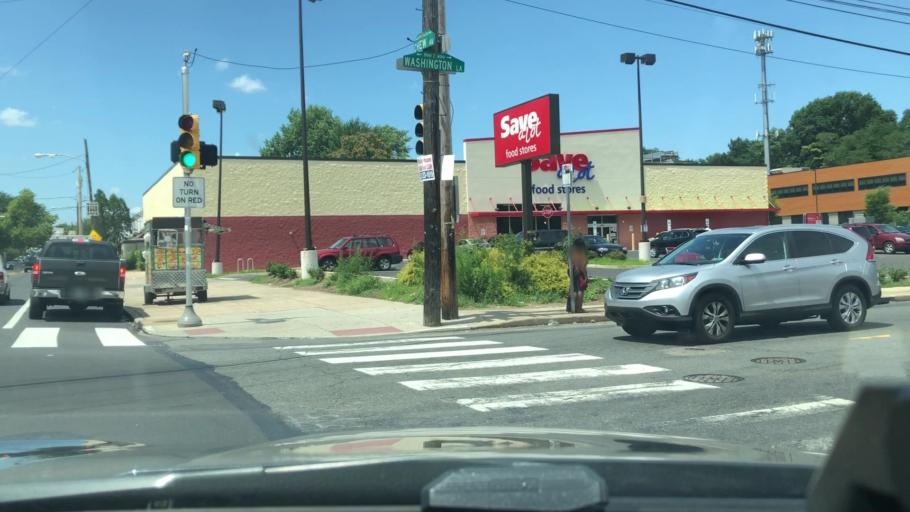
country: US
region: Pennsylvania
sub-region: Montgomery County
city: Wyndmoor
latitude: 40.0506
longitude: -75.1731
